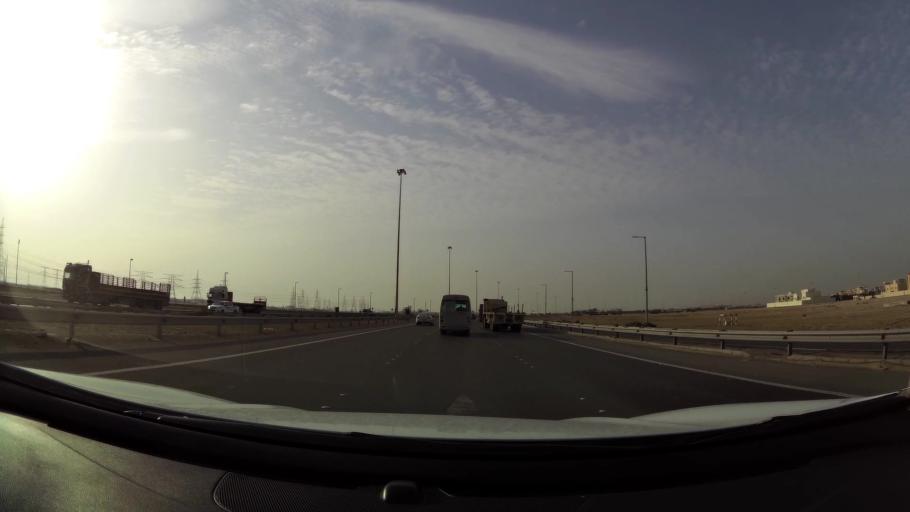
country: AE
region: Abu Dhabi
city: Abu Dhabi
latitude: 24.3059
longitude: 54.5316
